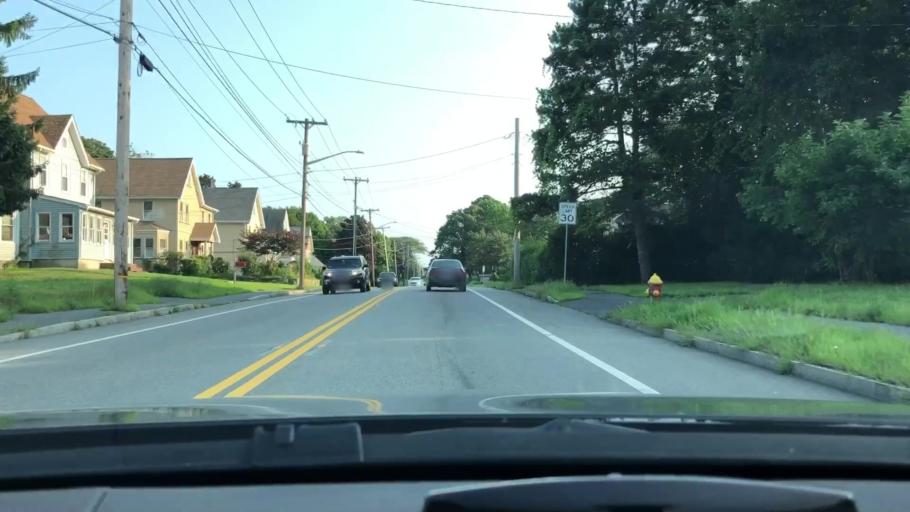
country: US
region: Massachusetts
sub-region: Norfolk County
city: Norwood
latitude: 42.2026
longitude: -71.1968
